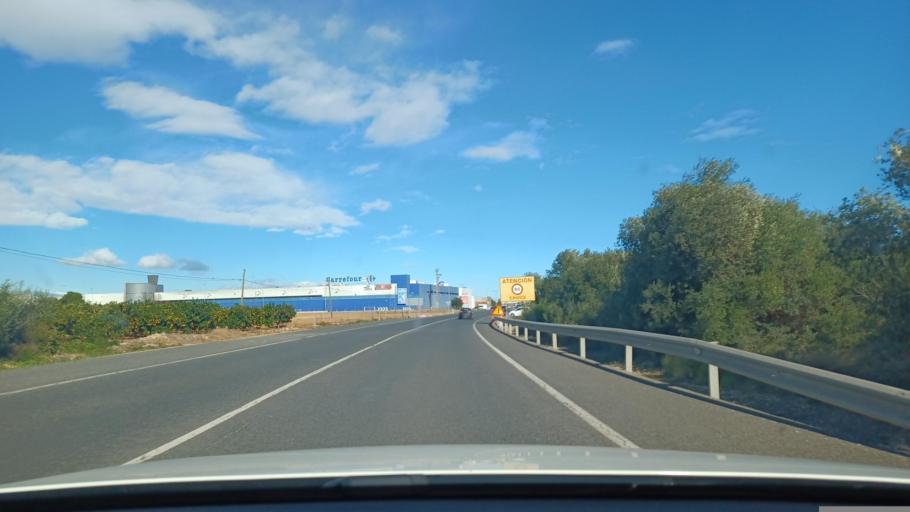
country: ES
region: Valencia
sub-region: Provincia de Castello
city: Vinaros
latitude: 40.4512
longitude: 0.4507
